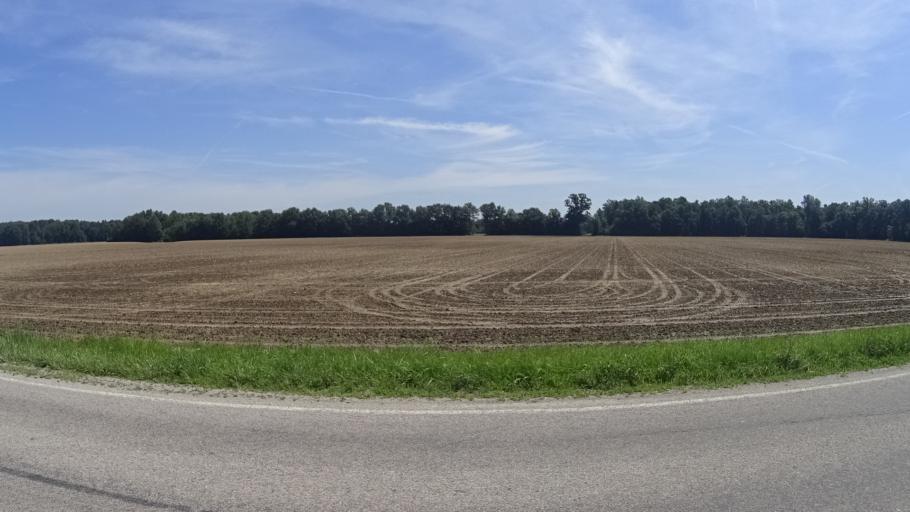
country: US
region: Ohio
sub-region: Erie County
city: Huron
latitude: 41.3420
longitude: -82.5102
